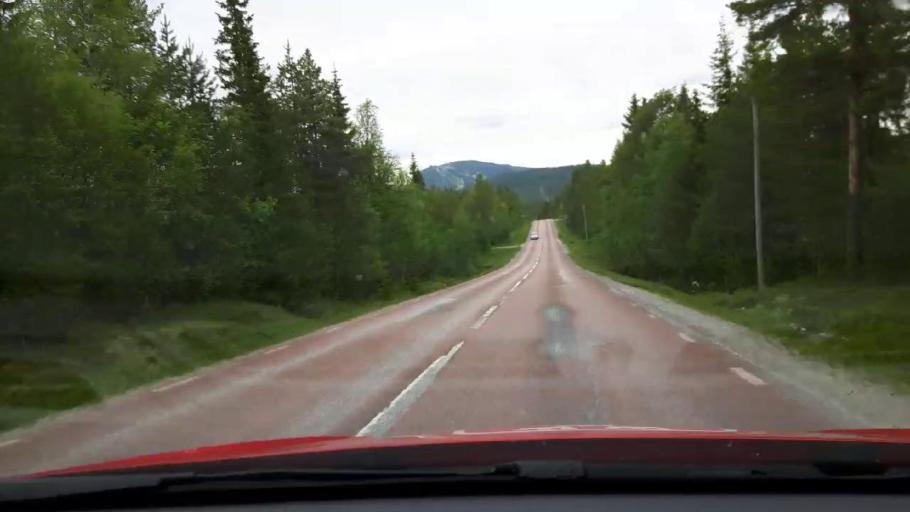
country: NO
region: Hedmark
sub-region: Engerdal
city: Engerdal
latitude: 62.5115
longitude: 12.6073
